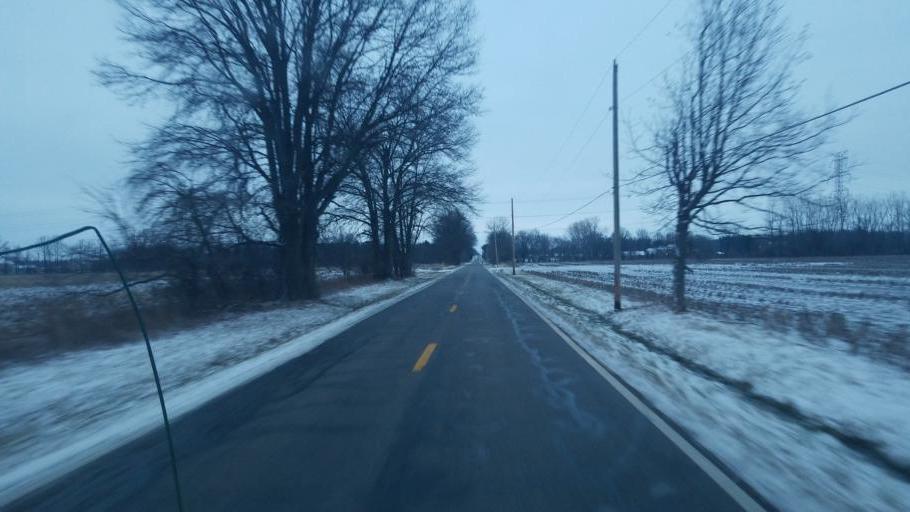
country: US
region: Ohio
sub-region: Delaware County
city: Sunbury
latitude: 40.1876
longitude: -82.8362
